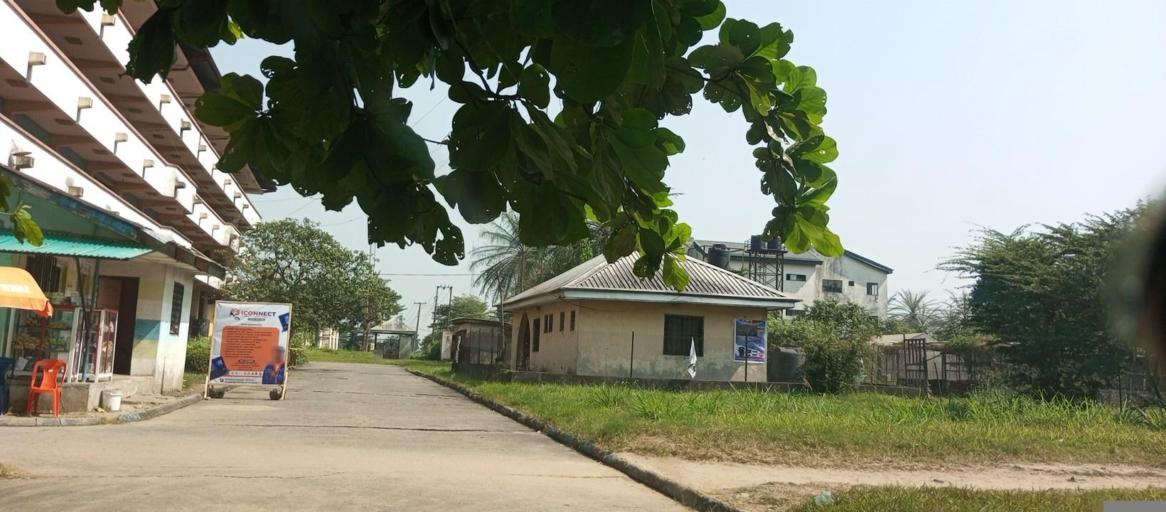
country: NG
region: Rivers
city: Emuoha
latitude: 4.9041
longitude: 6.9224
